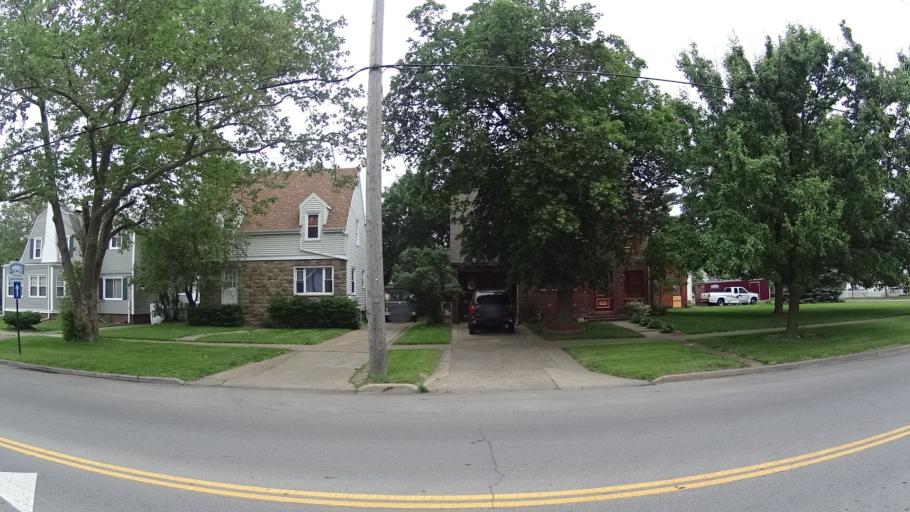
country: US
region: Ohio
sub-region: Erie County
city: Sandusky
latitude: 41.4334
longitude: -82.6984
